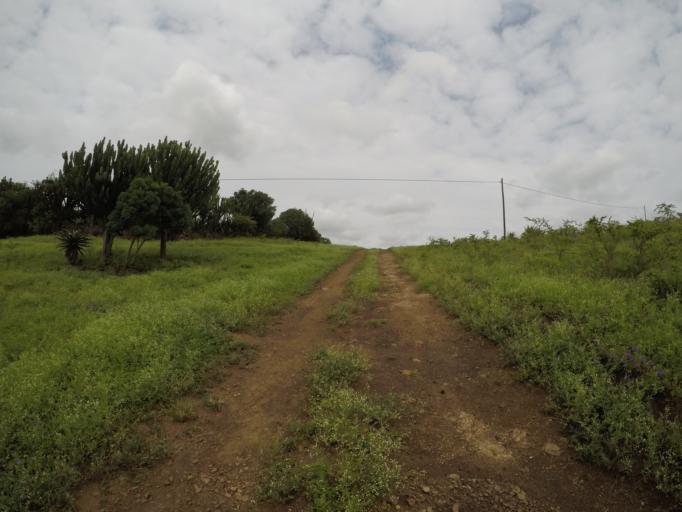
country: ZA
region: KwaZulu-Natal
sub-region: uThungulu District Municipality
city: Empangeni
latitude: -28.6109
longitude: 31.9000
